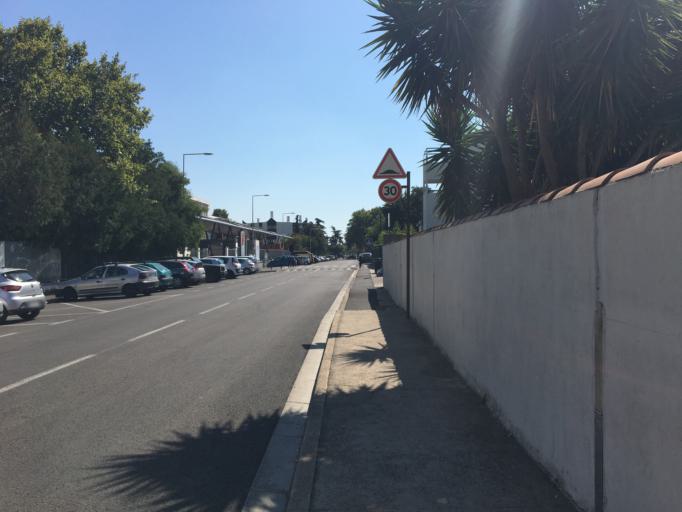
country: FR
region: Languedoc-Roussillon
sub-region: Departement du Gard
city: Nimes
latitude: 43.8236
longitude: 4.3588
